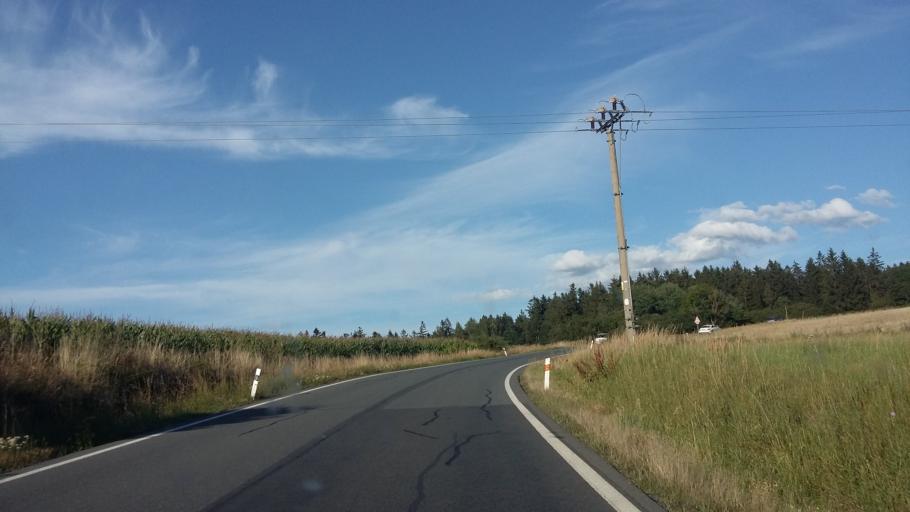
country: CZ
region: Plzensky
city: Mirosov
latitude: 49.6219
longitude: 13.6955
